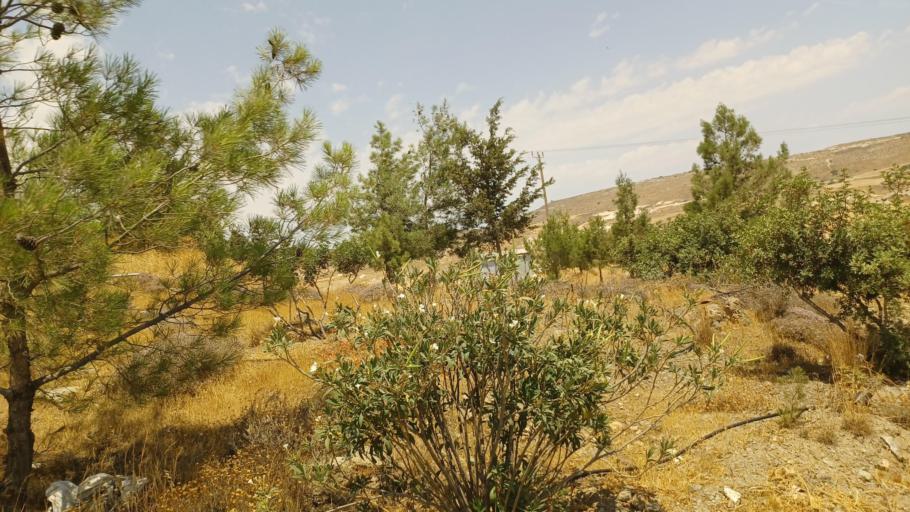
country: CY
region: Larnaka
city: Troulloi
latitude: 35.0276
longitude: 33.5950
